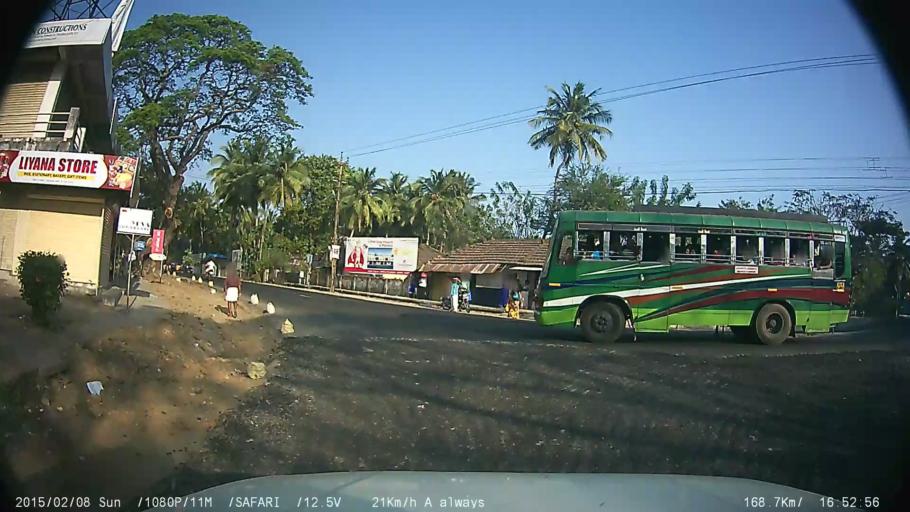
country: IN
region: Kerala
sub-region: Palakkad district
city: Palakkad
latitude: 10.7457
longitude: 76.6506
